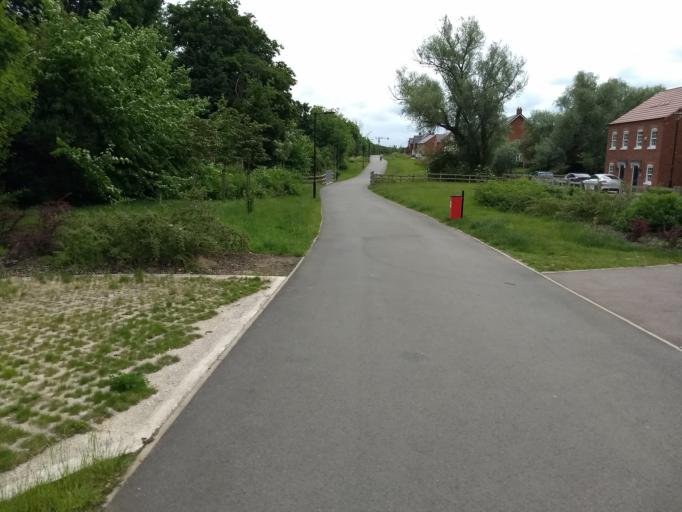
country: GB
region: England
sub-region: Bedford
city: Kempston
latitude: 52.1114
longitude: -0.5152
